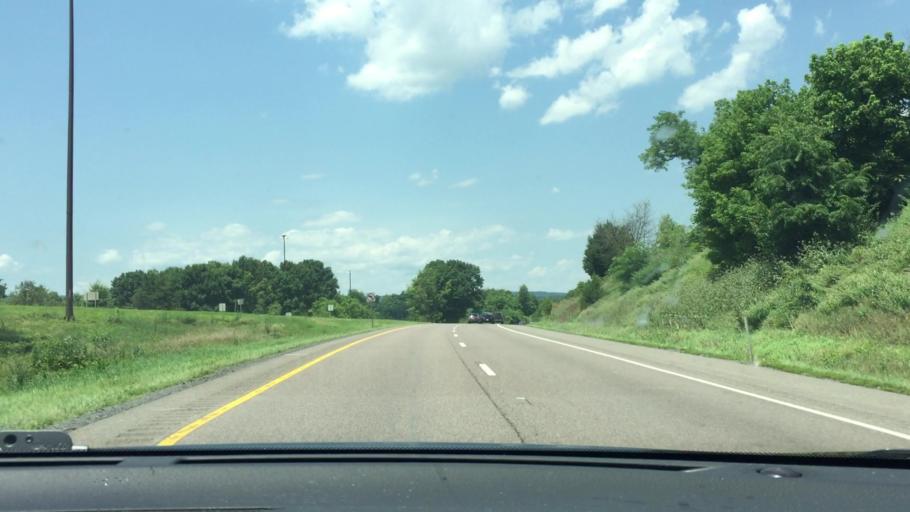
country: US
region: Maryland
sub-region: Washington County
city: Hancock
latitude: 39.7080
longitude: -78.1829
